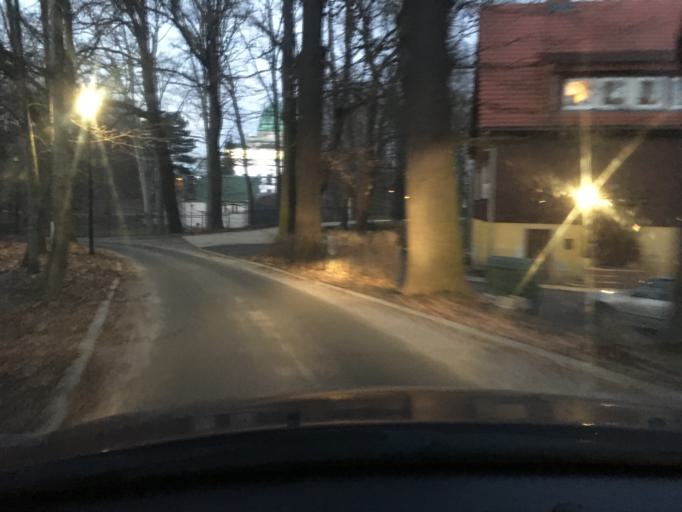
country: PL
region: Lower Silesian Voivodeship
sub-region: Powiat zgorzelecki
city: Zgorzelec
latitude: 51.1451
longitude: 15.0015
